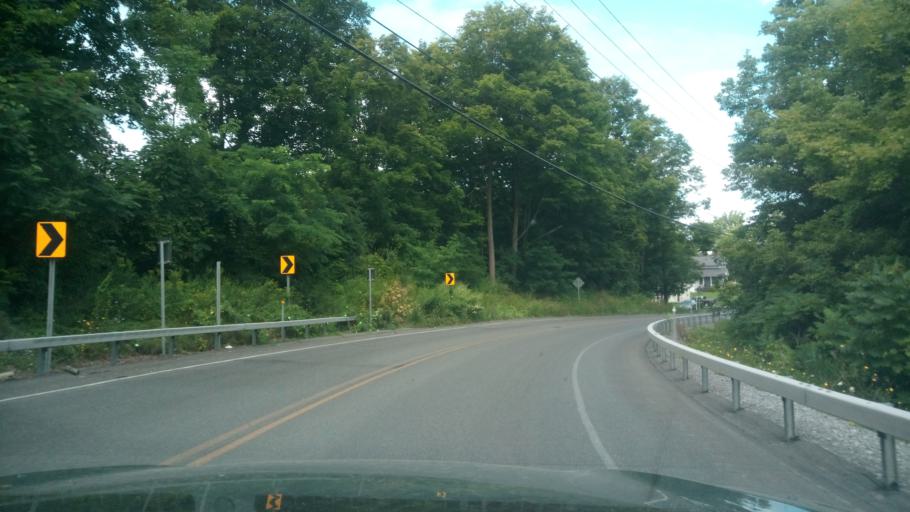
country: US
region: New York
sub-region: Onondaga County
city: East Syracuse
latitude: 42.9960
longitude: -76.0726
